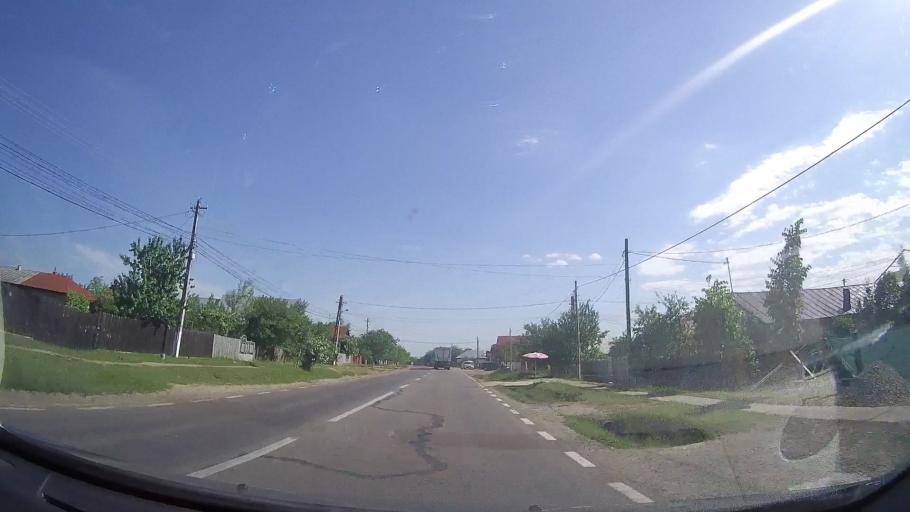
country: RO
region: Prahova
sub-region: Comuna Magurele
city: Magurele
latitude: 45.1192
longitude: 26.0338
